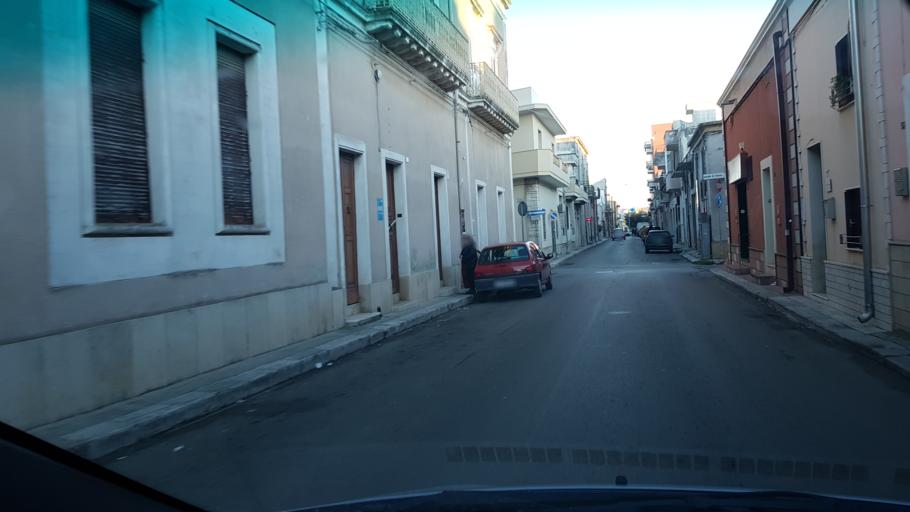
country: IT
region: Apulia
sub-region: Provincia di Brindisi
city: San Pietro Vernotico
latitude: 40.4864
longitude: 17.9996
